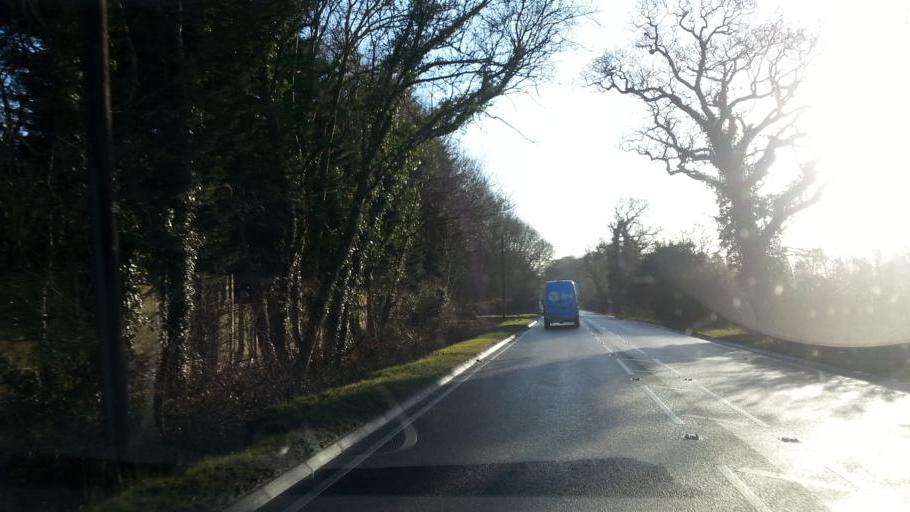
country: GB
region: England
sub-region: Nottinghamshire
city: South Collingham
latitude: 53.0811
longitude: -0.7215
